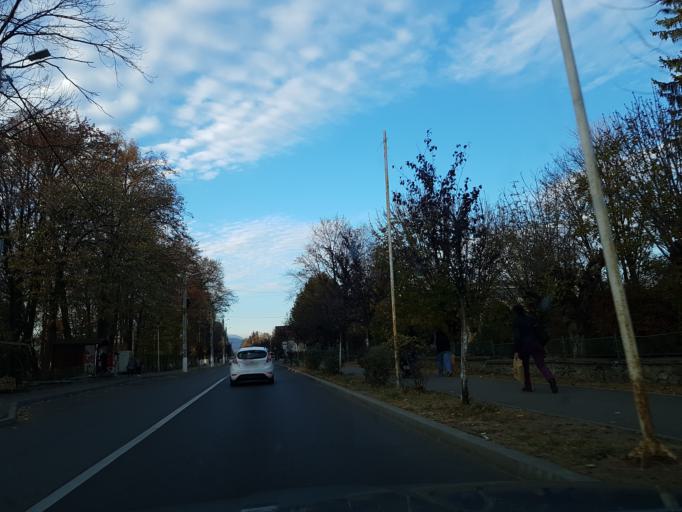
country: RO
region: Prahova
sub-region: Oras Breaza
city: Breaza
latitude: 45.1800
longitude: 25.6689
